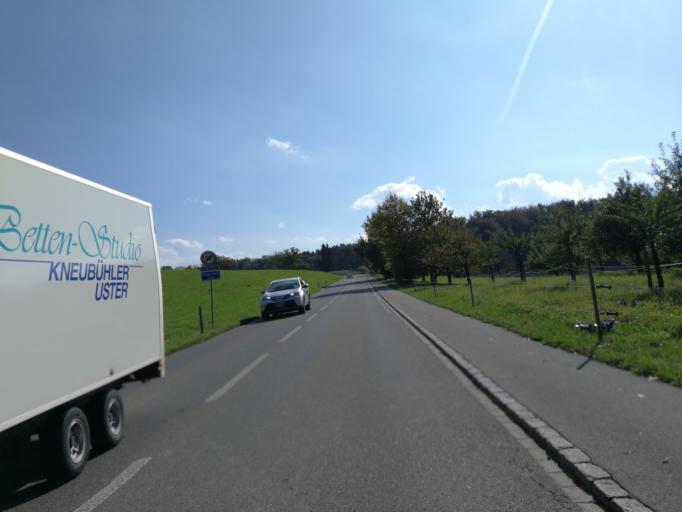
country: CH
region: Zurich
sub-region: Bezirk Meilen
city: Dorf
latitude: 47.2608
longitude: 8.7423
